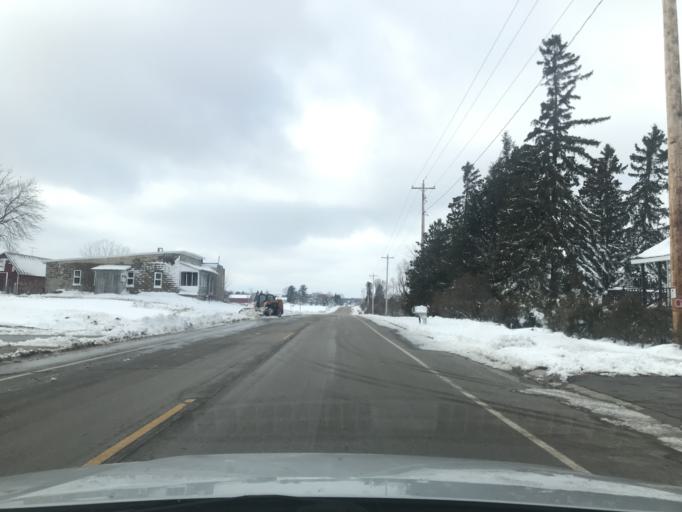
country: US
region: Wisconsin
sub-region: Oconto County
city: Oconto
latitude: 44.9497
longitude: -87.9447
